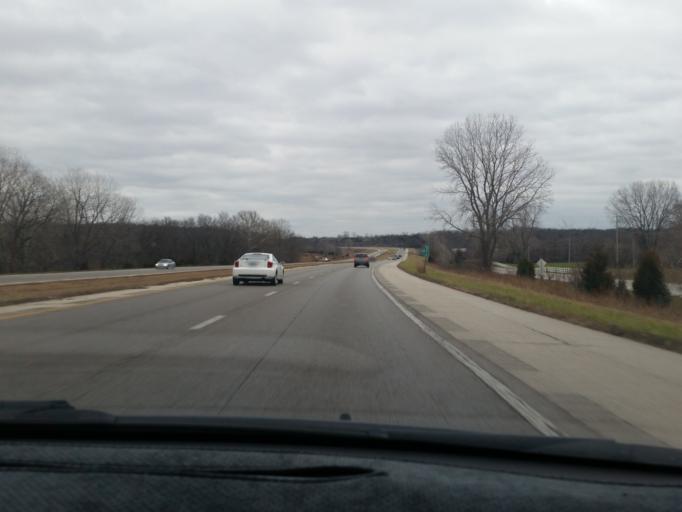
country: US
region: Kansas
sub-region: Johnson County
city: De Soto
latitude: 38.9547
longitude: -94.9119
